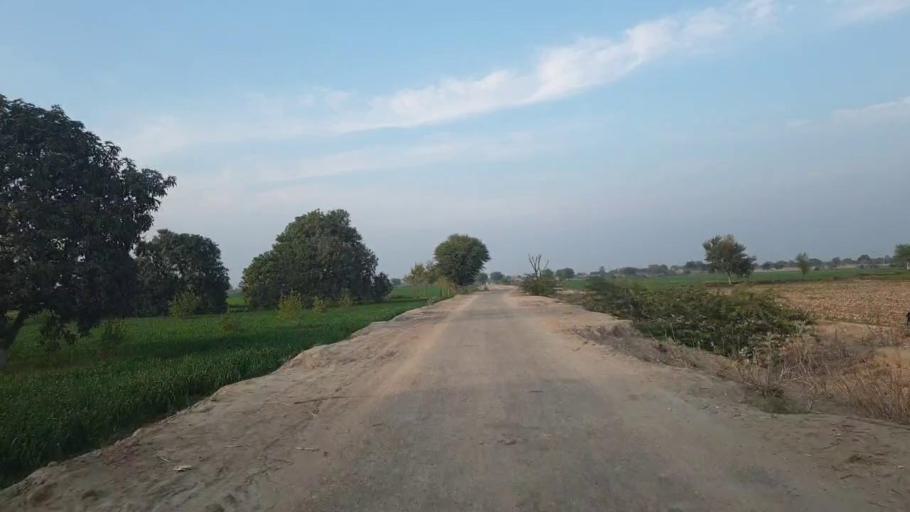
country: PK
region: Sindh
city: Shahpur Chakar
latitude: 26.1141
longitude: 68.5464
